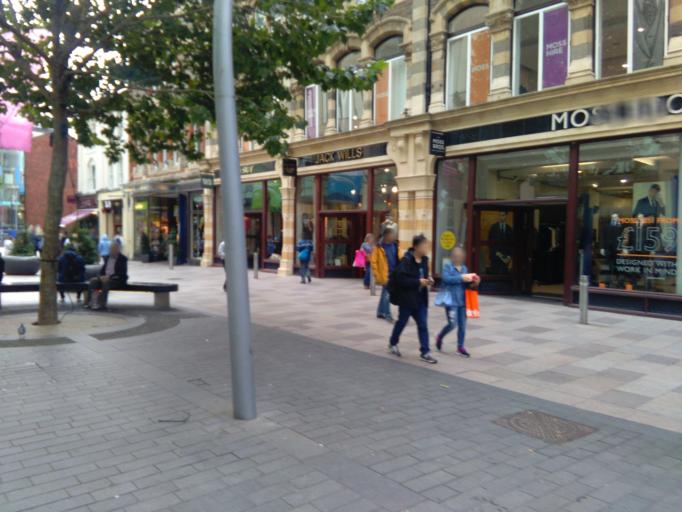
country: GB
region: Wales
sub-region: Cardiff
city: Cardiff
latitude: 51.4792
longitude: -3.1761
